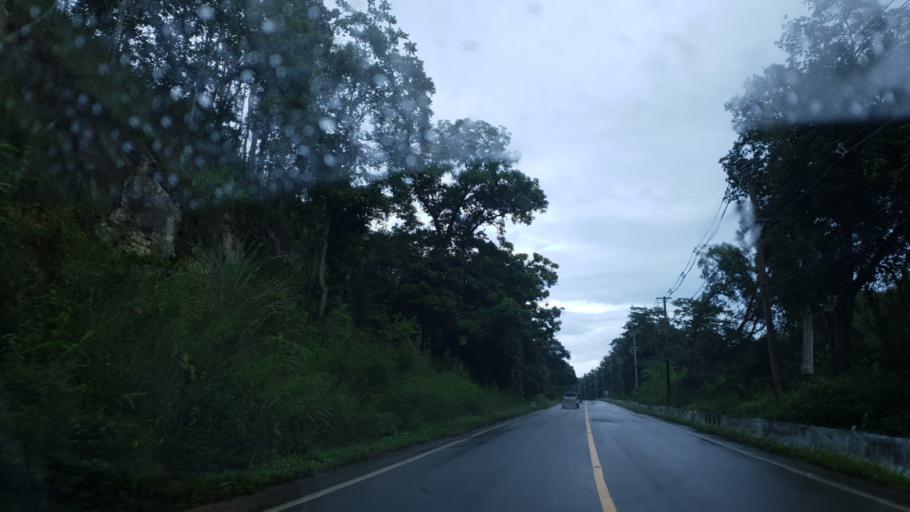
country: TH
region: Mae Hong Son
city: Ban Huai I Huak
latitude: 18.1473
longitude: 98.2040
